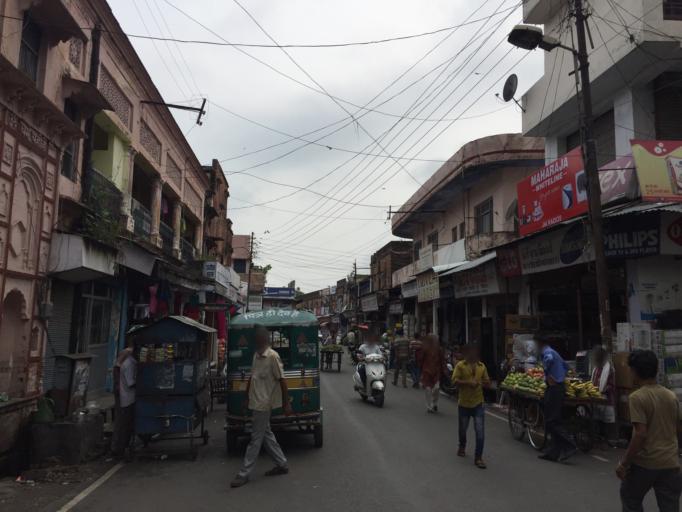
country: IN
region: Uttarakhand
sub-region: Dehradun
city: Rishikesh
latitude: 30.1070
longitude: 78.3004
